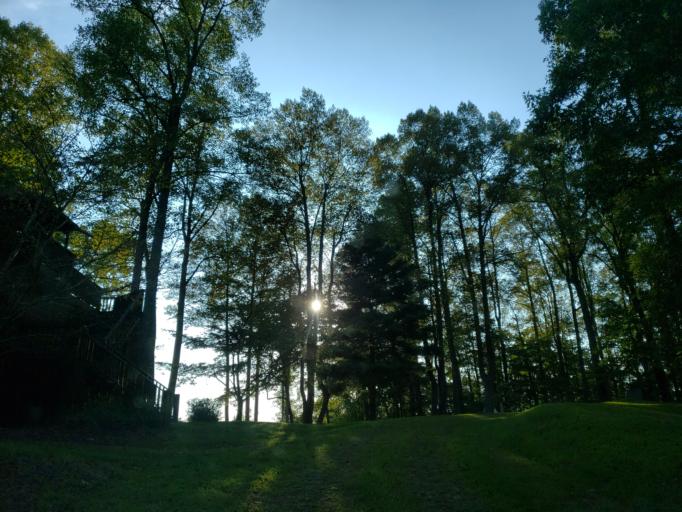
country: US
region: Georgia
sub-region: Fannin County
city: Blue Ridge
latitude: 34.6937
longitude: -84.2639
